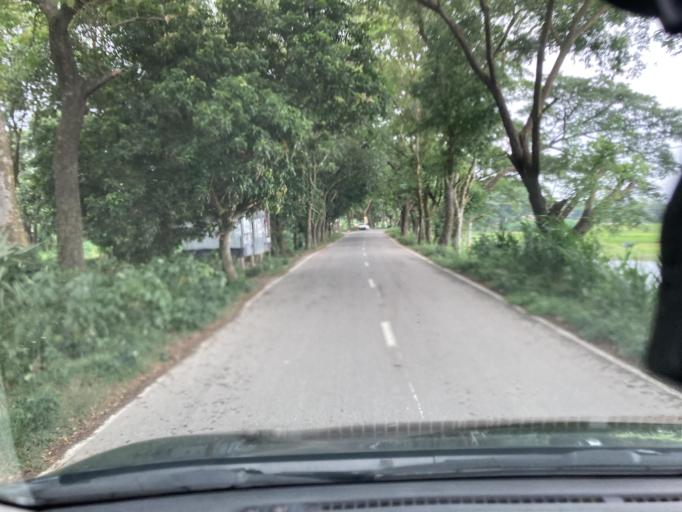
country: BD
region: Dhaka
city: Dohar
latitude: 23.7863
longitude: 90.0644
